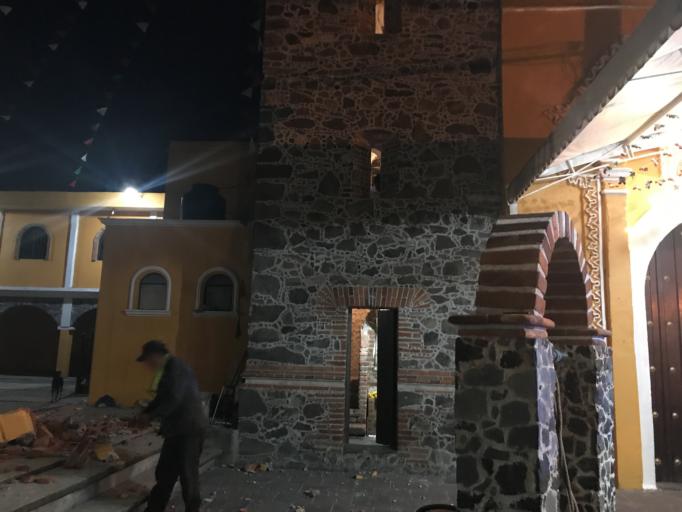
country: MX
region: Puebla
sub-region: San Gregorio Atzompa
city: Chipilo de Francisco Javier Mina
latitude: 19.0294
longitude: -98.3186
